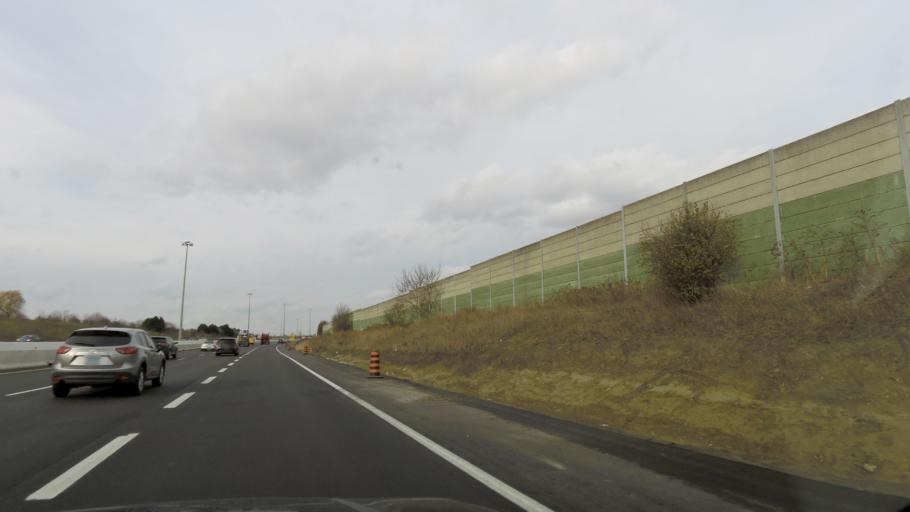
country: CA
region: Ontario
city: Etobicoke
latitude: 43.7274
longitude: -79.6248
